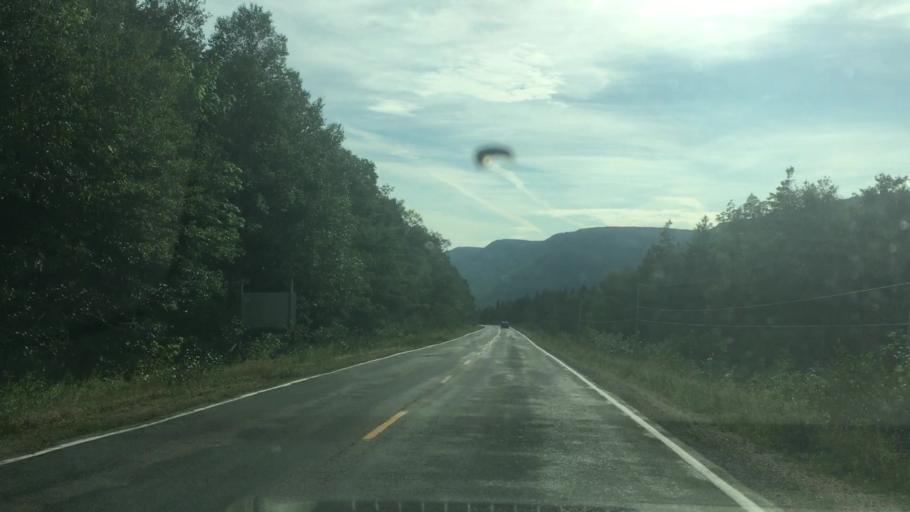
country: CA
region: Nova Scotia
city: Sydney Mines
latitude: 46.8669
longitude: -60.5576
